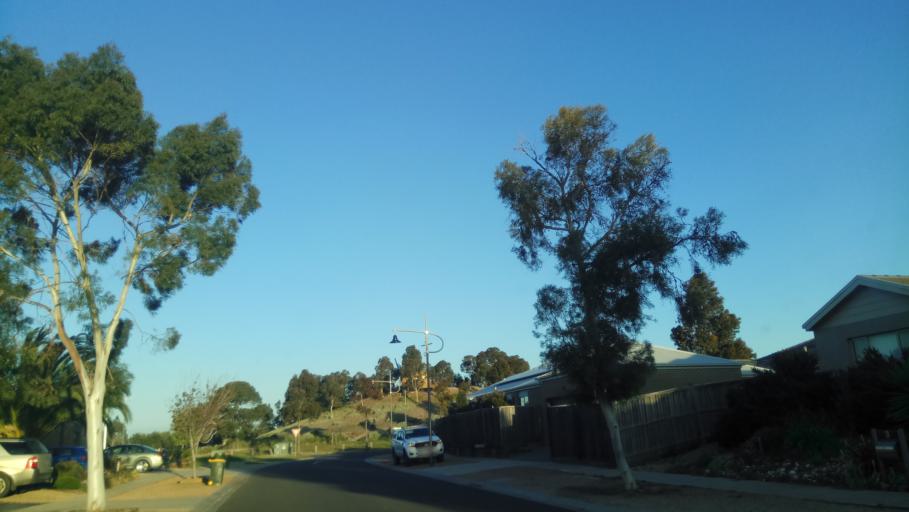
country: AU
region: Victoria
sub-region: Wyndham
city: Point Cook
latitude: -37.9037
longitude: 144.7418
